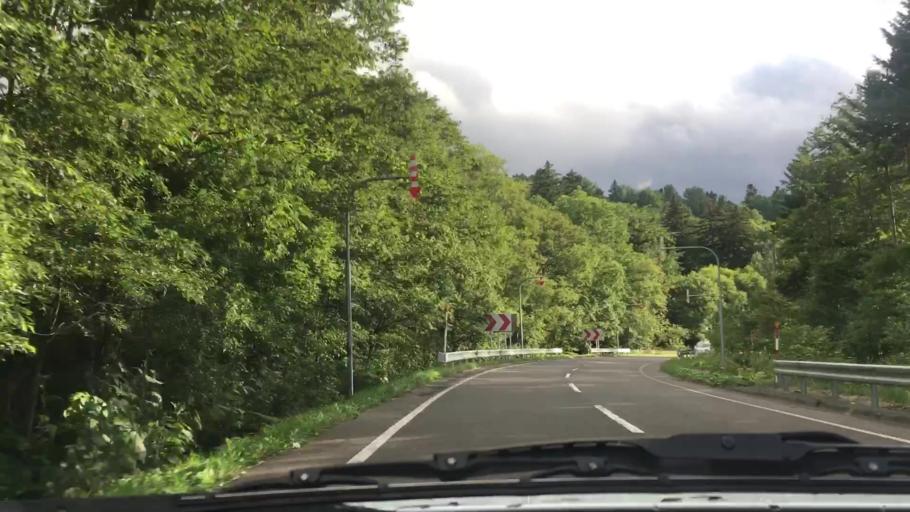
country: JP
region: Hokkaido
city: Shimo-furano
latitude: 43.0871
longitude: 142.6788
